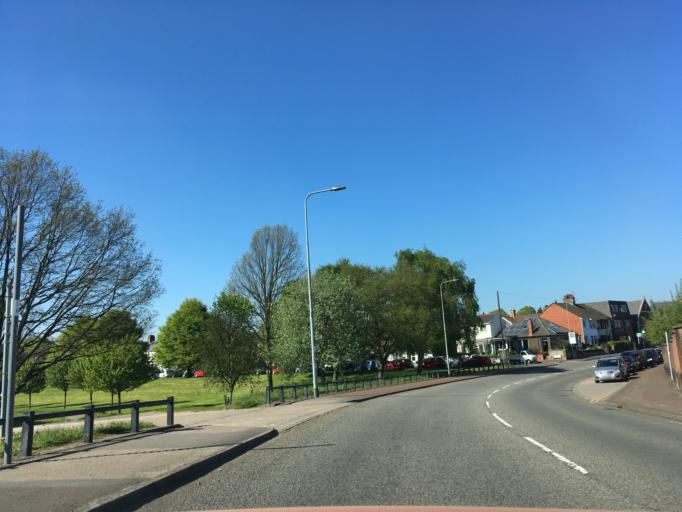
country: GB
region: Wales
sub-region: Cardiff
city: Radyr
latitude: 51.5009
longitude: -3.2277
